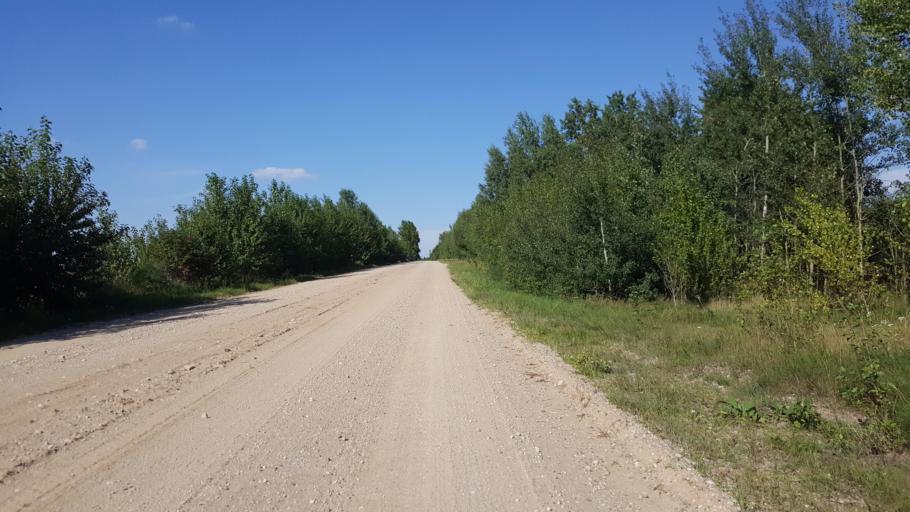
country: BY
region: Brest
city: Kamyanyets
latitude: 52.3509
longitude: 23.6892
